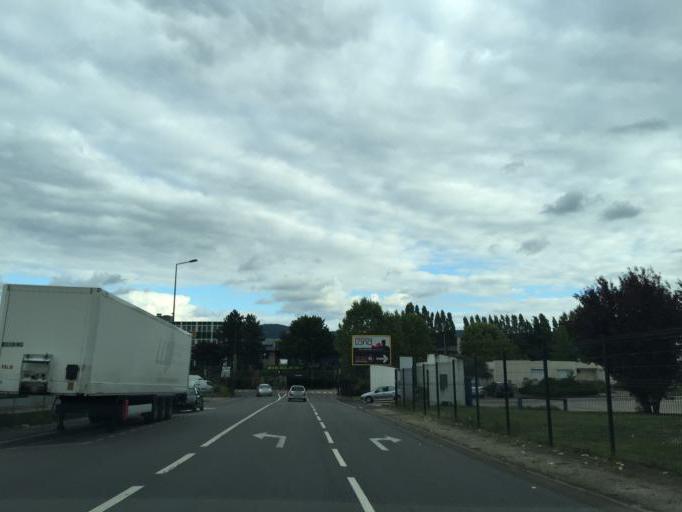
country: FR
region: Rhone-Alpes
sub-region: Departement de la Loire
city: Saint-Etienne
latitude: 45.4542
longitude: 4.4094
